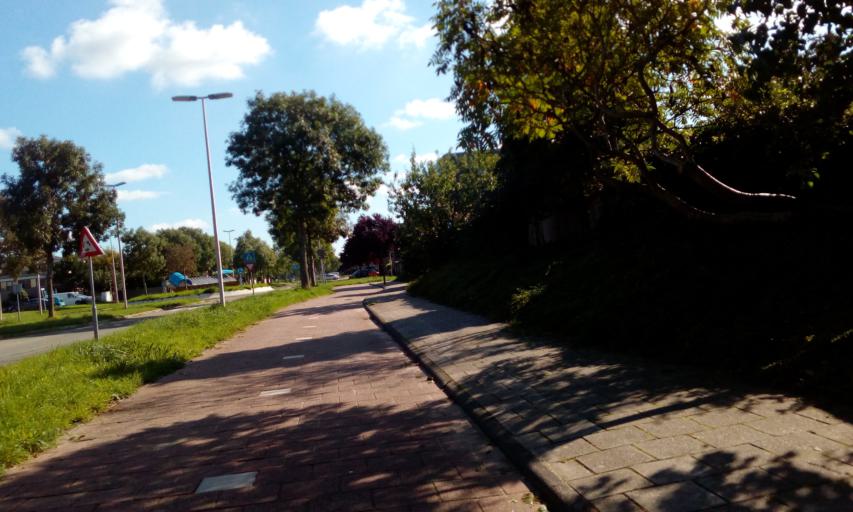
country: NL
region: South Holland
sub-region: Gemeente Zoetermeer
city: Zoetermeer
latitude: 52.0783
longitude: 4.5124
